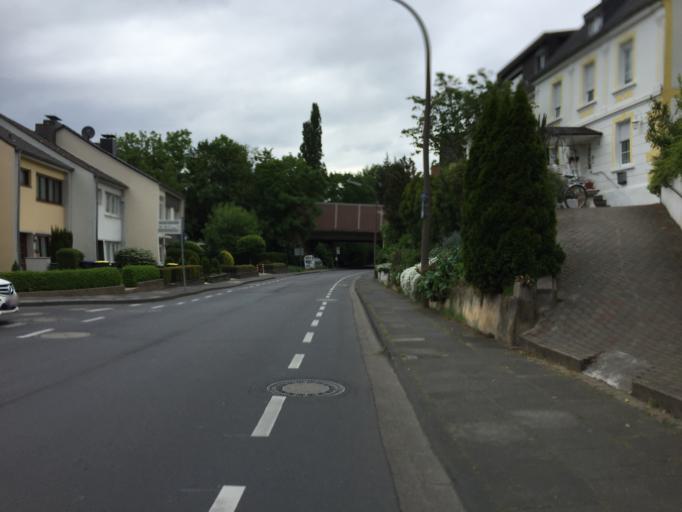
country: DE
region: North Rhine-Westphalia
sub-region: Regierungsbezirk Koln
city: Bonn
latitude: 50.7170
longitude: 7.0715
